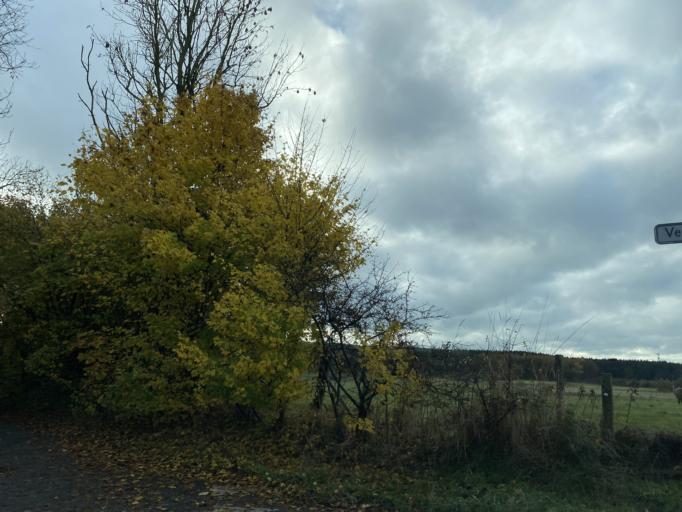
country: DK
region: Central Jutland
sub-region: Skanderborg Kommune
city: Skovby
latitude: 56.2229
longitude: 9.9574
